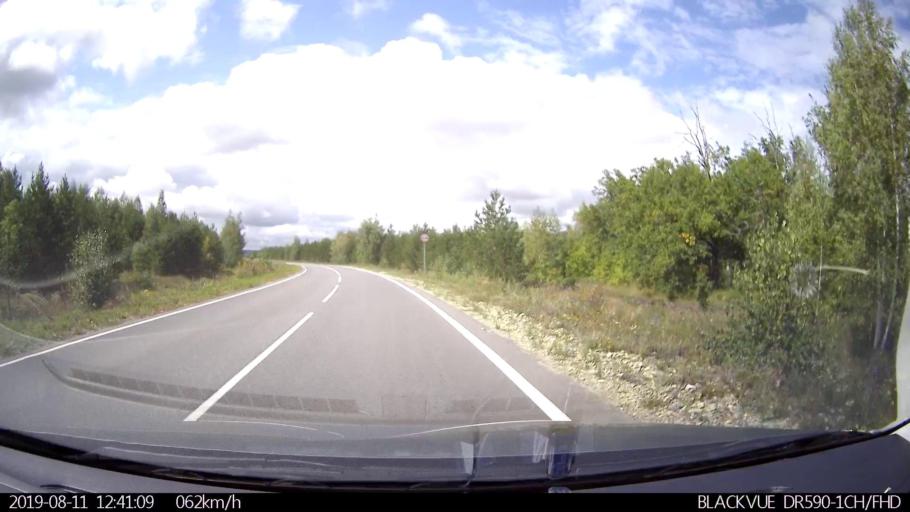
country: RU
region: Ulyanovsk
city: Ignatovka
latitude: 53.8424
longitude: 47.7707
